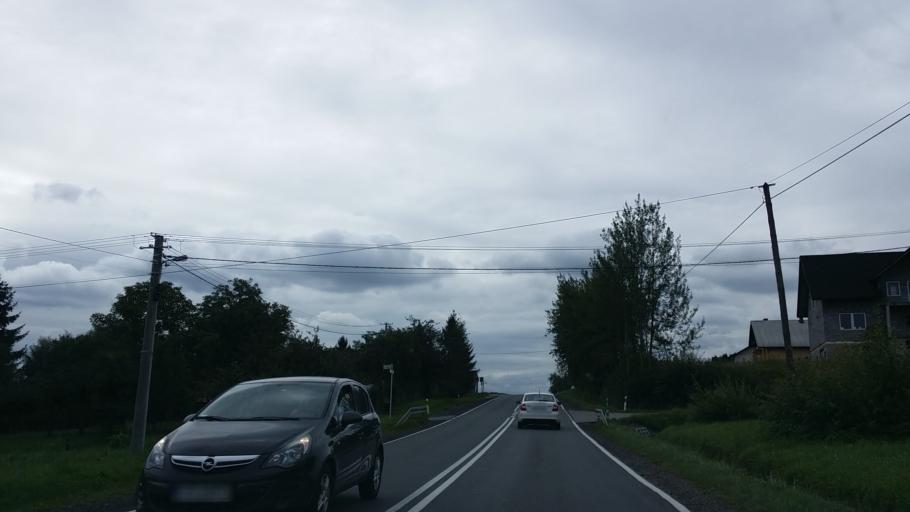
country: PL
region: Lesser Poland Voivodeship
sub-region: Powiat wadowicki
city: Radocza
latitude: 49.9251
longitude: 19.4764
